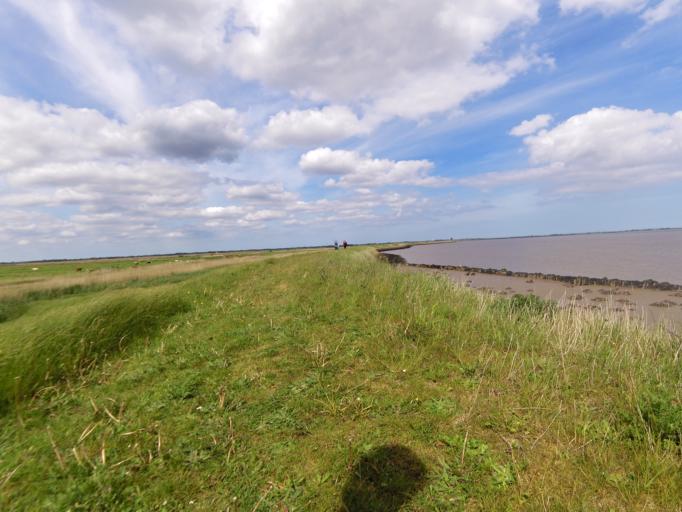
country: GB
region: England
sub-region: Norfolk
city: Great Yarmouth
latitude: 52.5978
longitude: 1.6528
